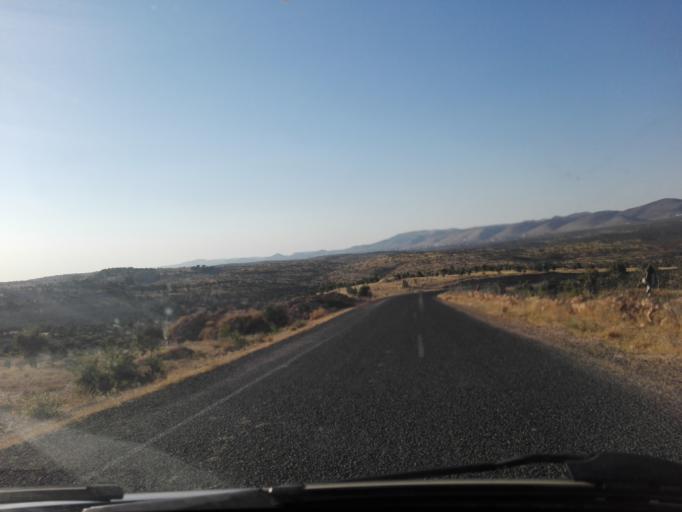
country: TR
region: Mardin
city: Kilavuz
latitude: 37.4995
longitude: 41.7630
